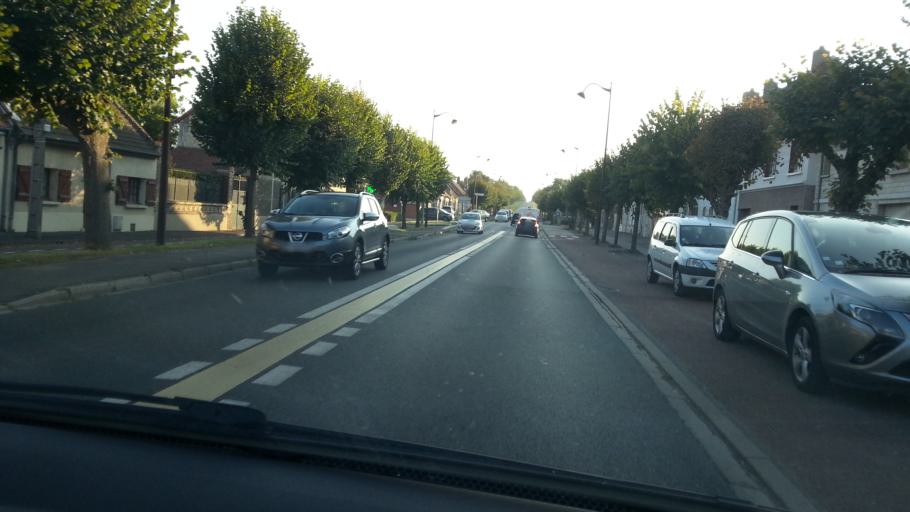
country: FR
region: Picardie
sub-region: Departement de l'Oise
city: Estrees-Saint-Denis
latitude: 49.4240
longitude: 2.6366
